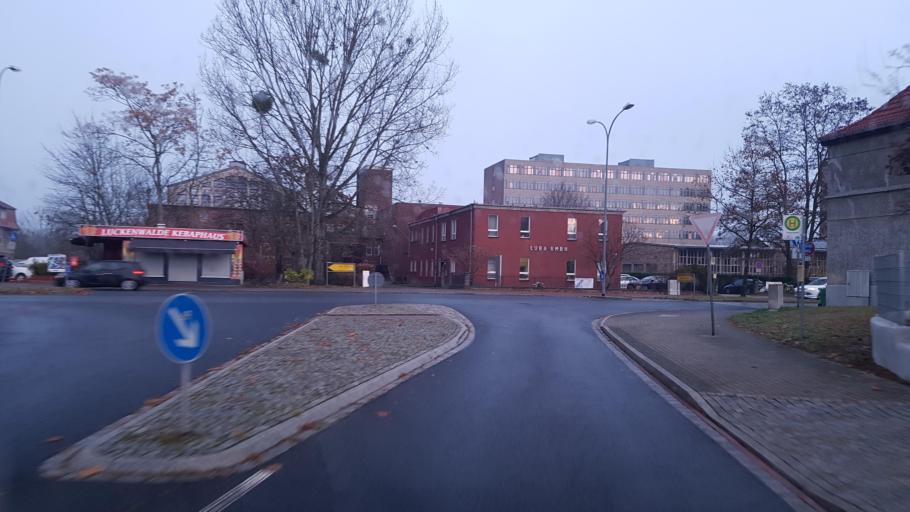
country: DE
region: Brandenburg
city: Luckenwalde
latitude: 52.0830
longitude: 13.1554
